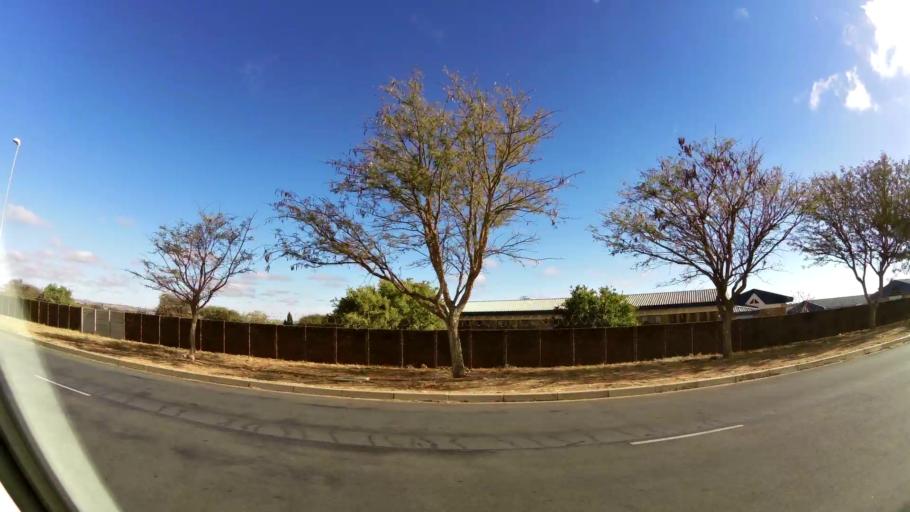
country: ZA
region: Limpopo
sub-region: Capricorn District Municipality
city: Polokwane
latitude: -23.9212
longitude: 29.4753
